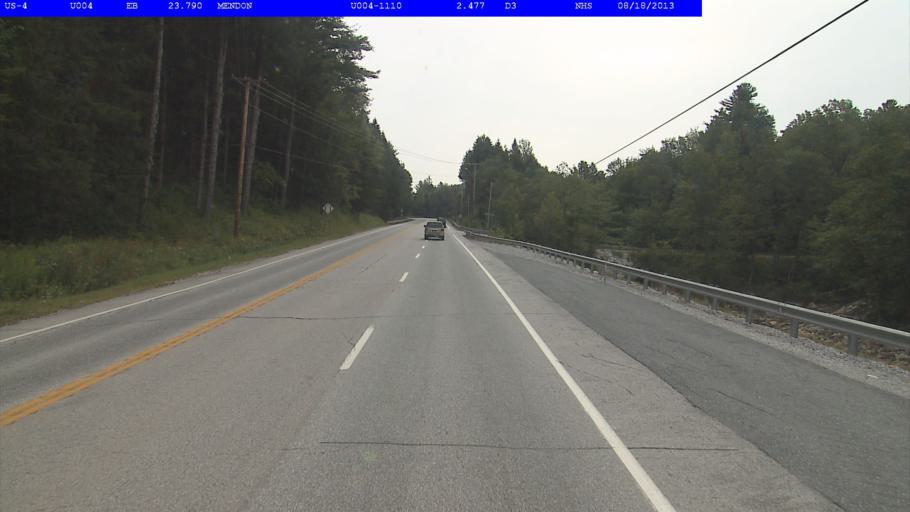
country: US
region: Vermont
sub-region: Rutland County
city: Rutland
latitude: 43.6483
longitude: -72.9046
